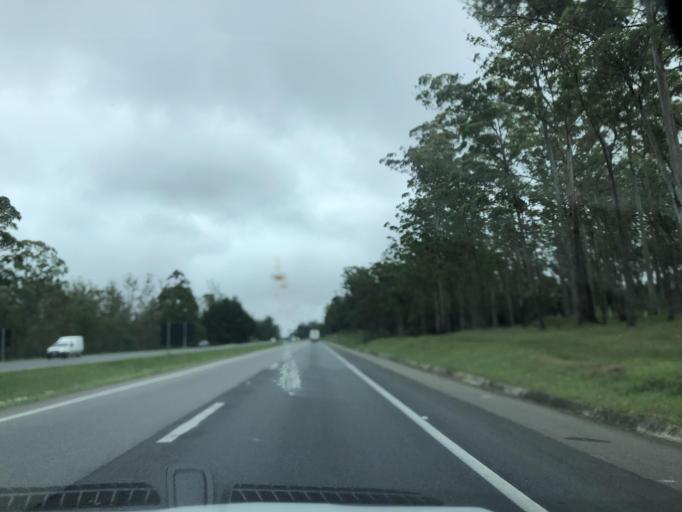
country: BR
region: Parana
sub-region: Piraquara
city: Piraquara
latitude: -25.4286
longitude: -49.0811
